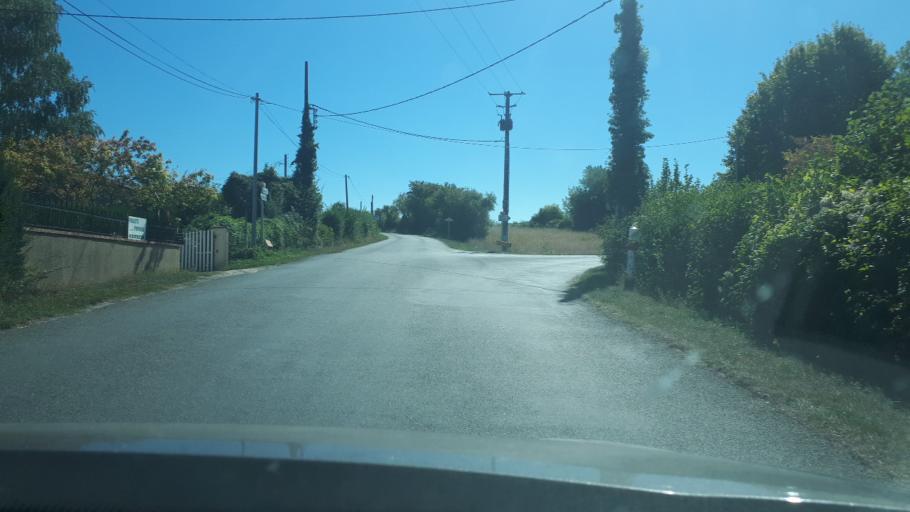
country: FR
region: Centre
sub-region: Departement du Cher
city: Sancerre
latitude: 47.2518
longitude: 2.7609
